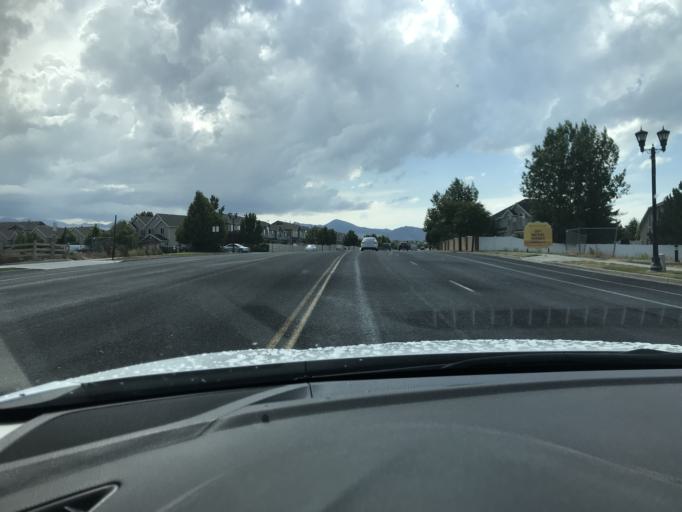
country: US
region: Utah
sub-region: Salt Lake County
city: South Jordan Heights
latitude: 40.5619
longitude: -111.9813
